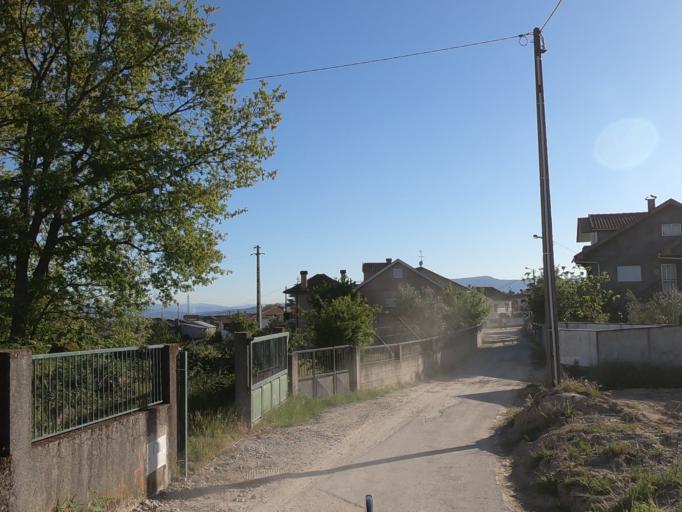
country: PT
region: Vila Real
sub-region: Vila Real
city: Vila Real
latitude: 41.3298
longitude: -7.6907
